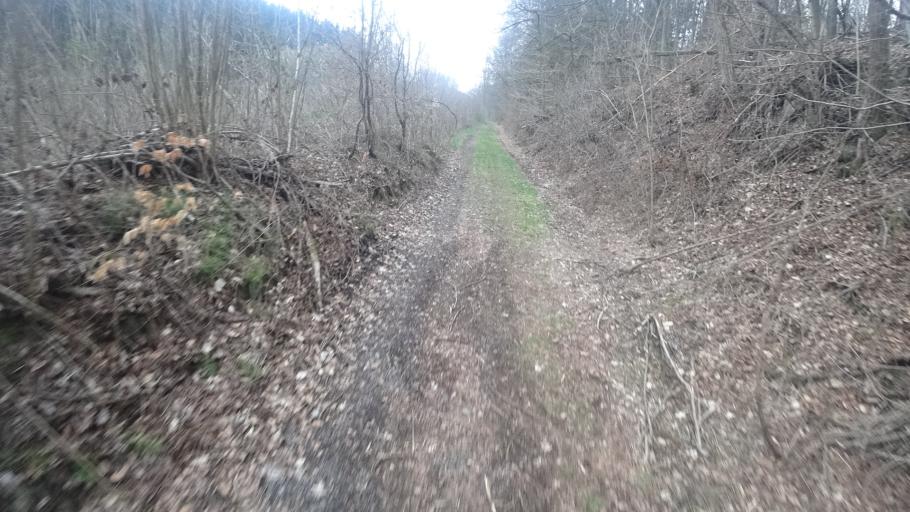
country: DE
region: Rheinland-Pfalz
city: Elben
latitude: 50.7477
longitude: 7.8318
